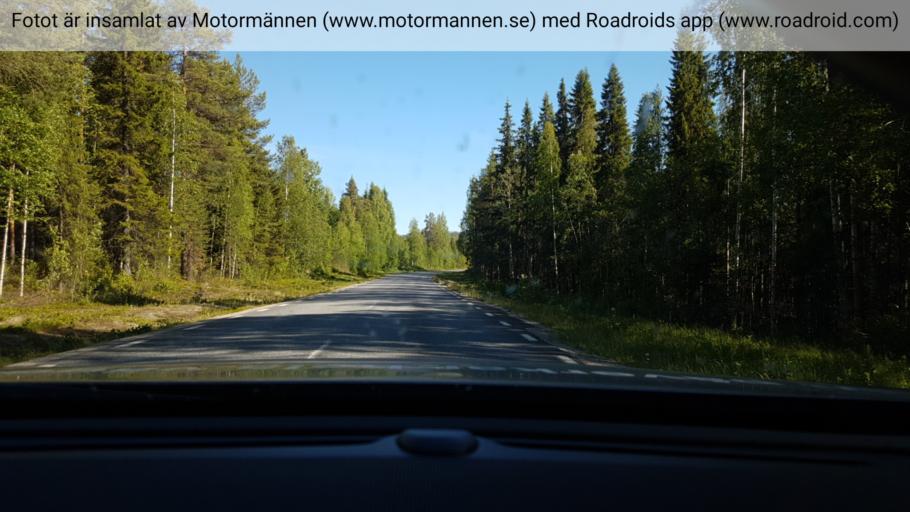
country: SE
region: Vaesterbotten
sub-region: Lycksele Kommun
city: Lycksele
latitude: 64.4486
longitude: 18.9369
